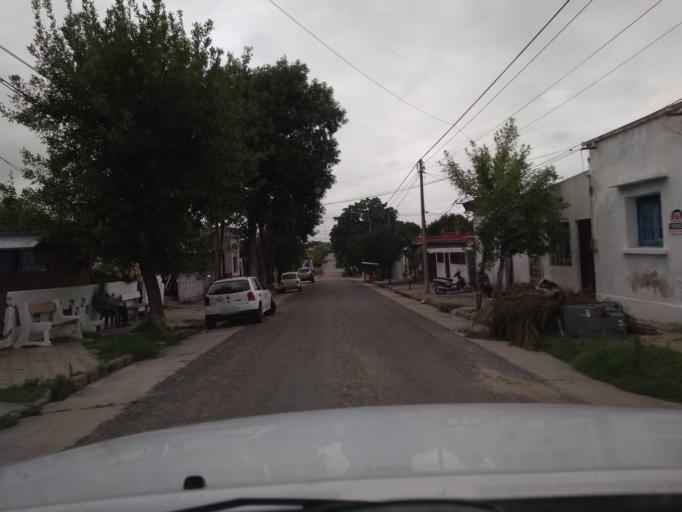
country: UY
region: Florida
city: Florida
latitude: -34.1049
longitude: -56.2105
